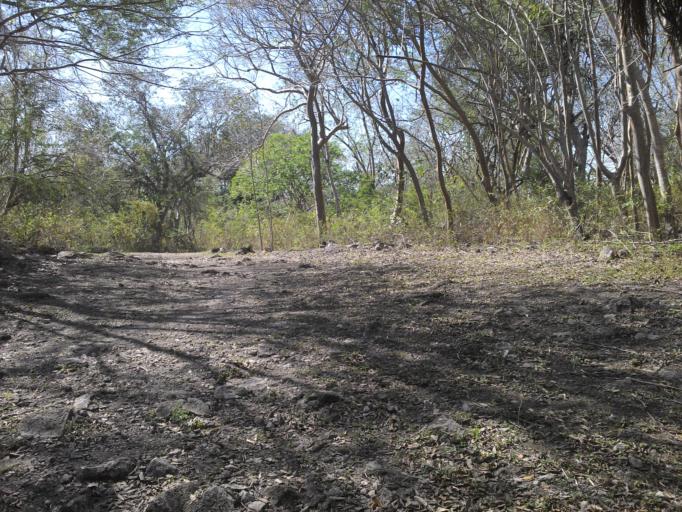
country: MX
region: Yucatan
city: Tekoh
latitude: 20.6290
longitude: -89.4590
